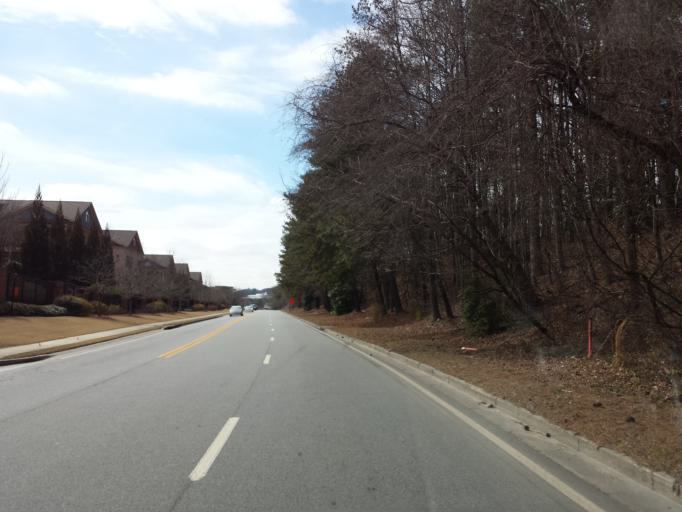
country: US
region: Georgia
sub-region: Cobb County
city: Vinings
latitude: 33.9035
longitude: -84.4362
